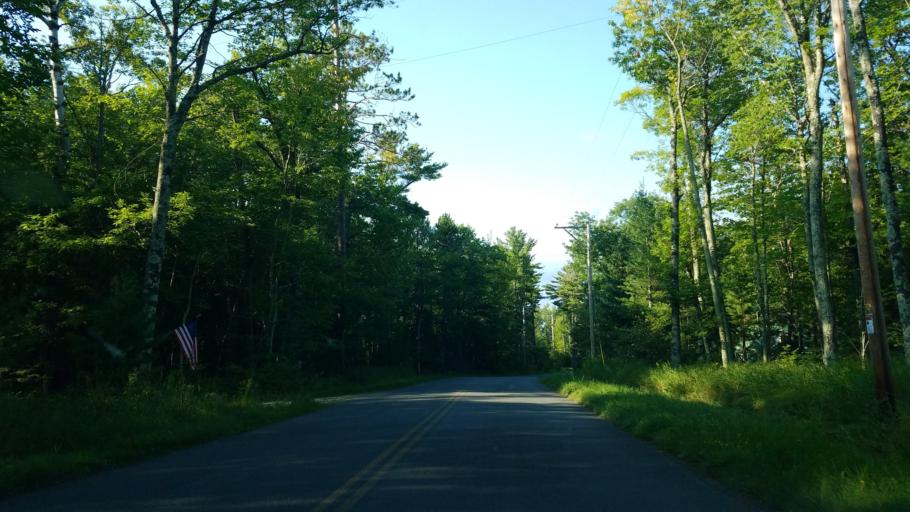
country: US
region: Wisconsin
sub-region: Bayfield County
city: Washburn
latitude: 46.7646
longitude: -90.7808
